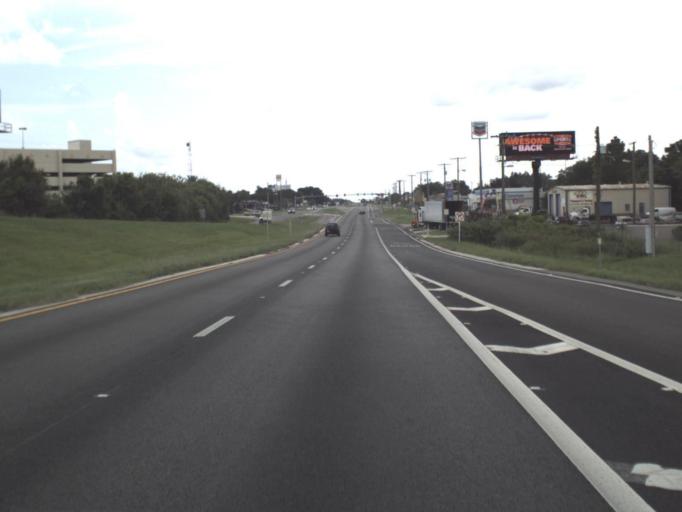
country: US
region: Florida
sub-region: Hillsborough County
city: East Lake-Orient Park
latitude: 27.9963
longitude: -82.3679
